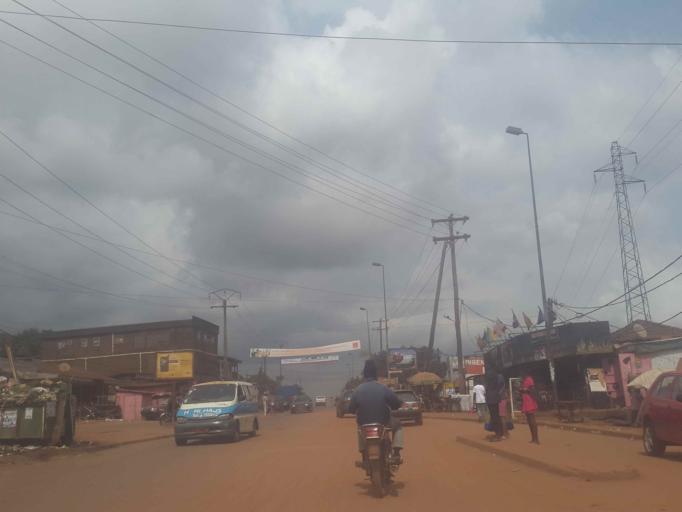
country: CM
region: Centre
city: Yaounde
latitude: 3.8754
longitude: 11.4741
